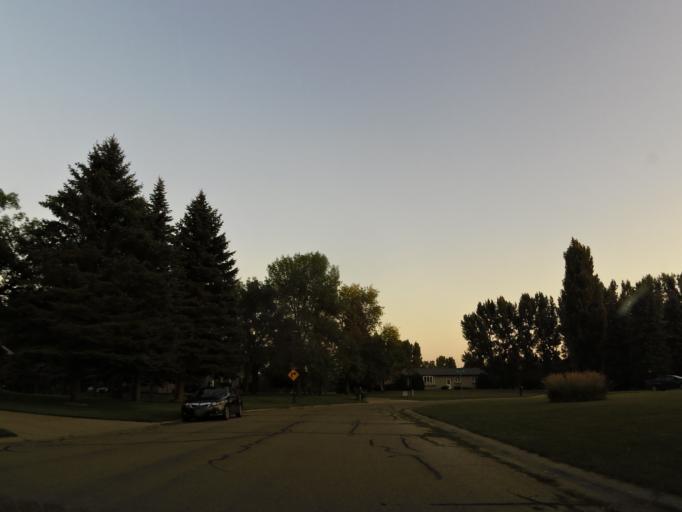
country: US
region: North Dakota
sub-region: Grand Forks County
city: Grand Forks
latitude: 47.8542
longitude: -97.0076
